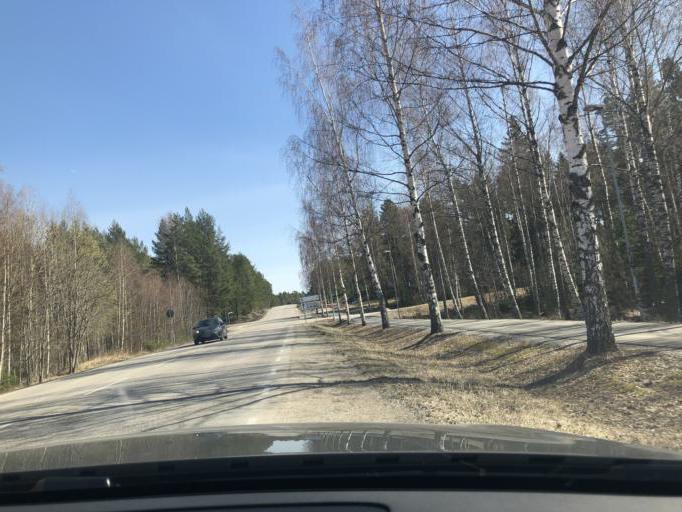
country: SE
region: Gaevleborg
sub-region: Hudiksvalls Kommun
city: Hudiksvall
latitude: 61.7247
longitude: 17.1579
